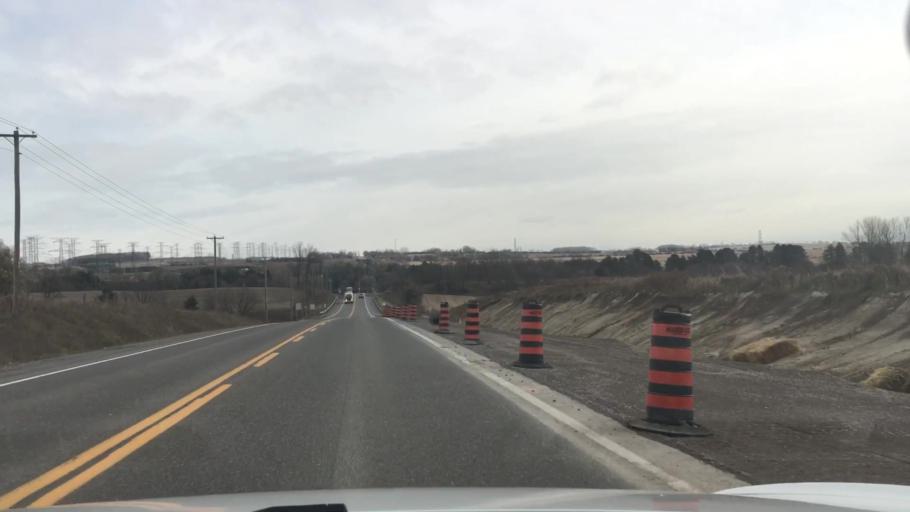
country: CA
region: Ontario
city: Oshawa
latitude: 43.9692
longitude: -78.8943
